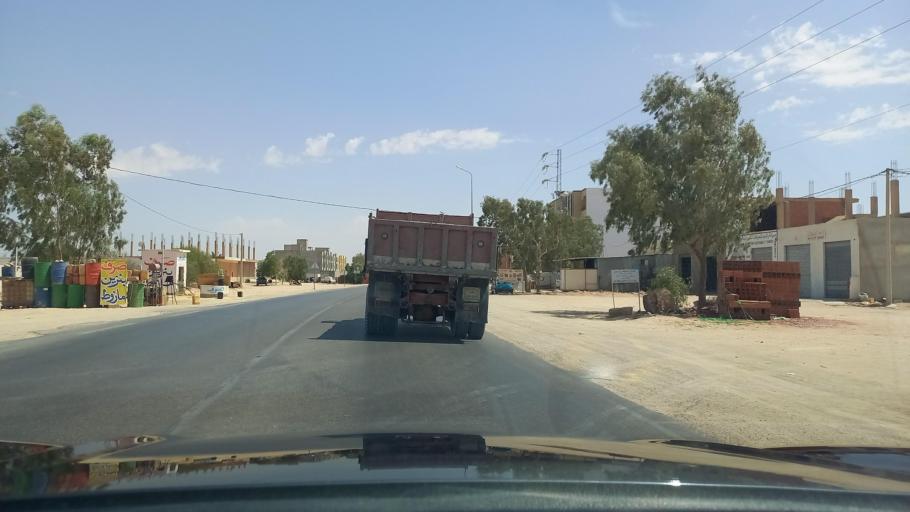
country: TN
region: Madanin
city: Medenine
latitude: 33.3668
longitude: 10.4559
